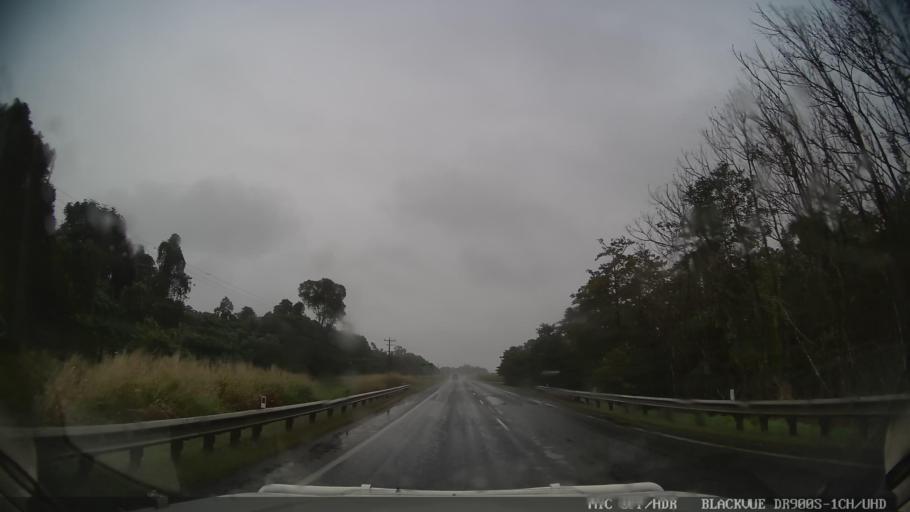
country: AU
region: Queensland
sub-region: Cassowary Coast
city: Innisfail
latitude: -17.7540
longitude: 146.0278
